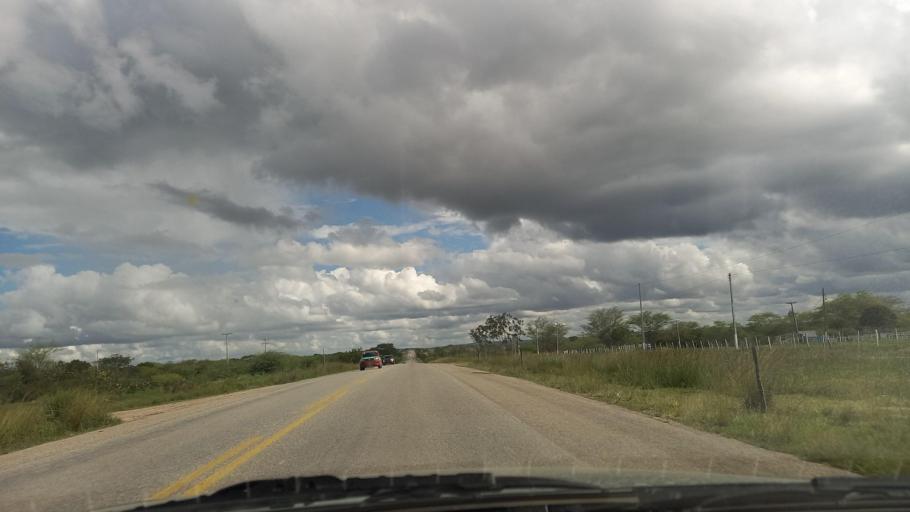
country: BR
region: Pernambuco
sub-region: Cachoeirinha
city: Cachoeirinha
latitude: -8.5088
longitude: -36.2510
